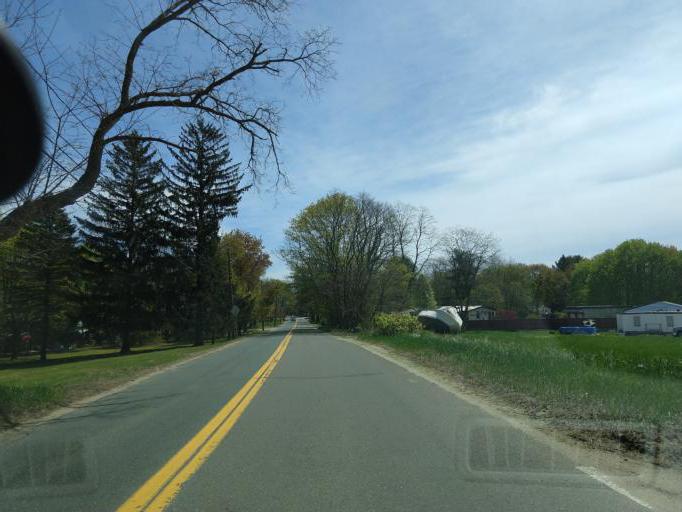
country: US
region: New Hampshire
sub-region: Rockingham County
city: Seabrook
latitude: 42.8677
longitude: -70.8842
